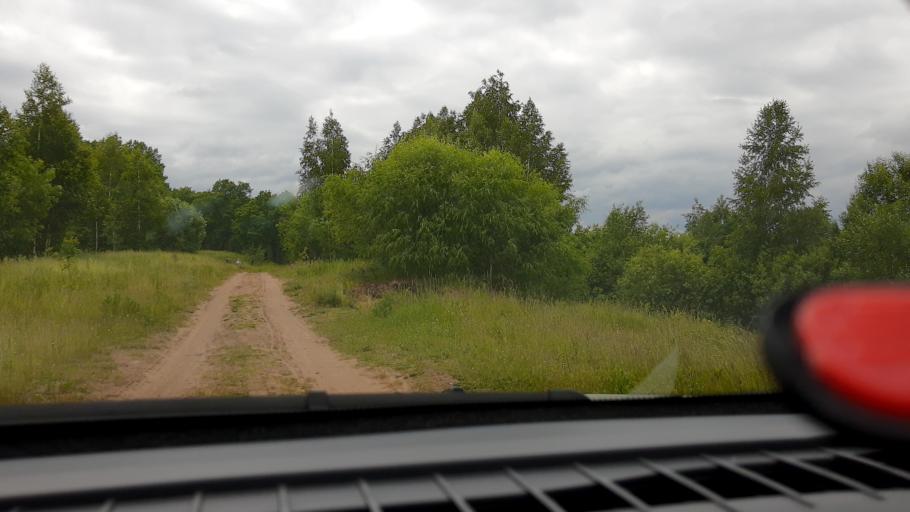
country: RU
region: Nizjnij Novgorod
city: Burevestnik
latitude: 56.2096
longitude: 43.8380
